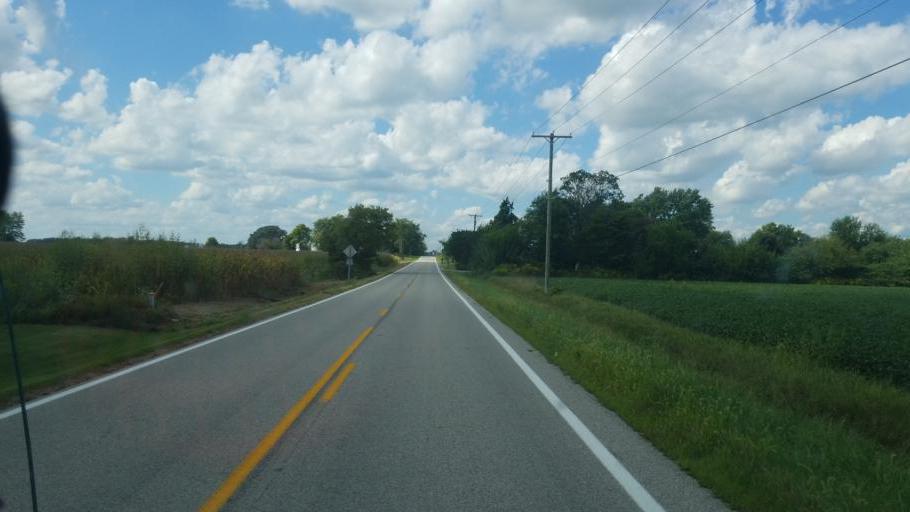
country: US
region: Ohio
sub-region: Union County
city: Richwood
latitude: 40.3691
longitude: -83.2659
